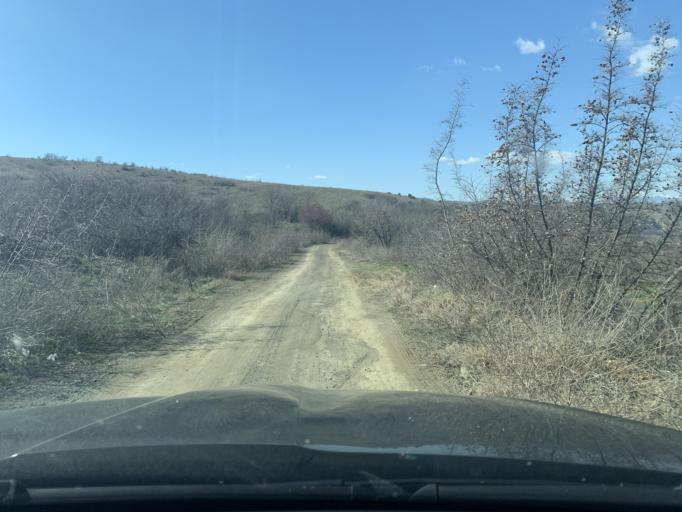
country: MK
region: Demir Kapija
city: Demir Kapija
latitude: 41.4139
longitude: 22.2155
